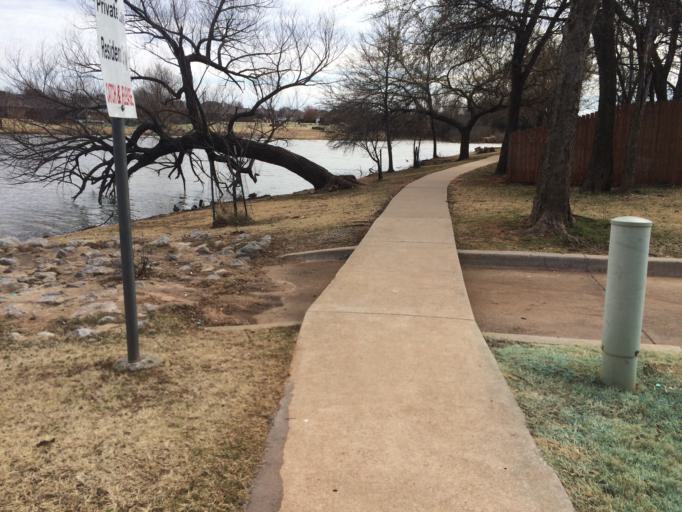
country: US
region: Oklahoma
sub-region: Cleveland County
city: Hall Park
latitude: 35.2231
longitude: -97.4028
